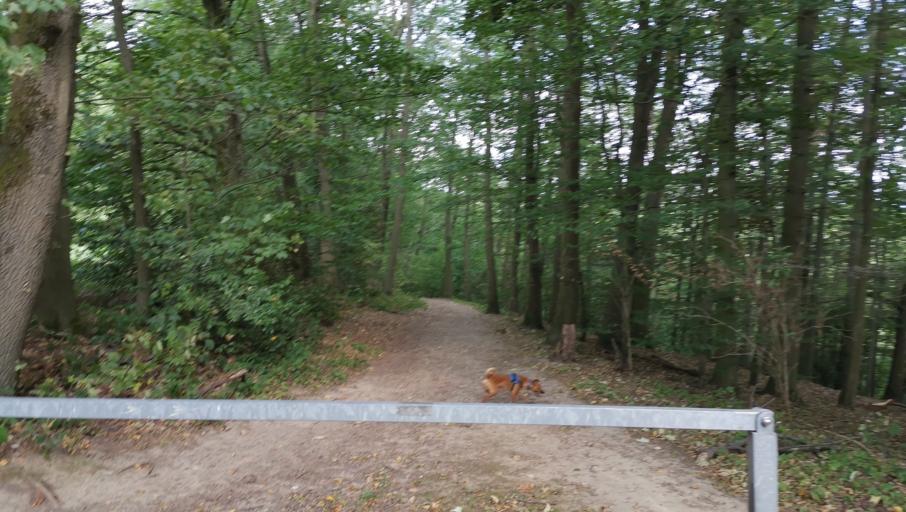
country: DE
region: North Rhine-Westphalia
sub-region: Regierungsbezirk Dusseldorf
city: Solingen
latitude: 51.1608
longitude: 7.1275
